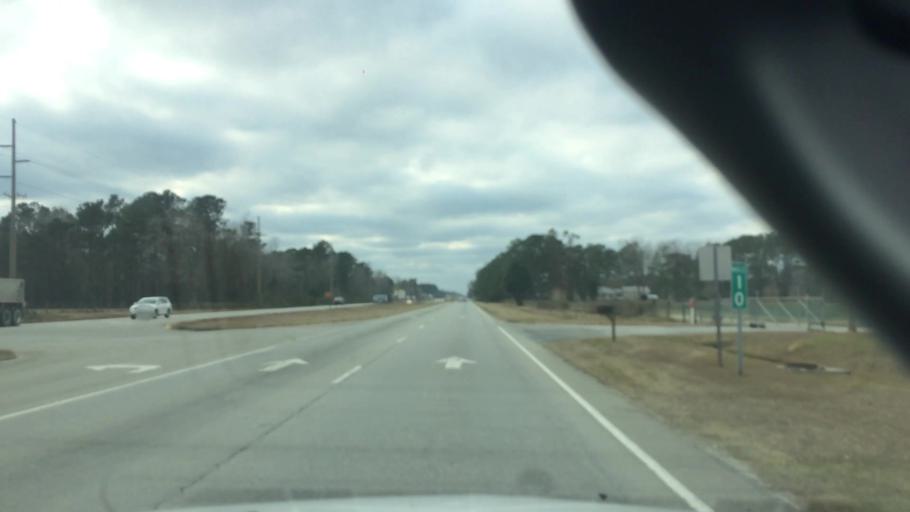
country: US
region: North Carolina
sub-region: Brunswick County
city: Shallotte
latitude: 33.9543
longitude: -78.4515
